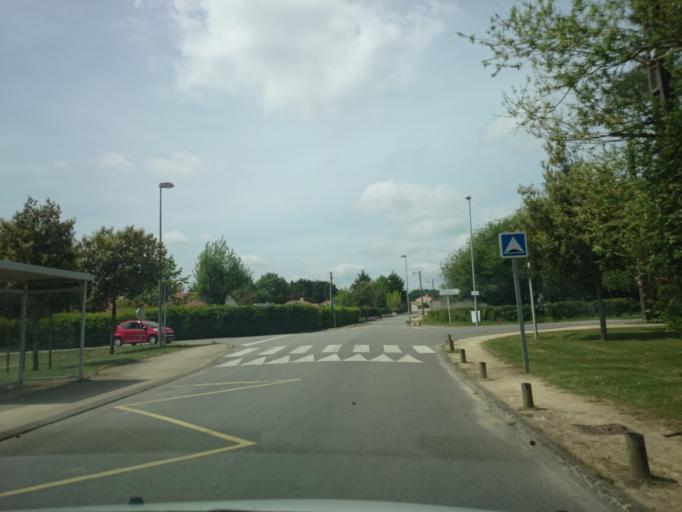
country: FR
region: Pays de la Loire
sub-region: Departement de la Loire-Atlantique
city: Bouaye
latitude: 47.1262
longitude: -1.6469
